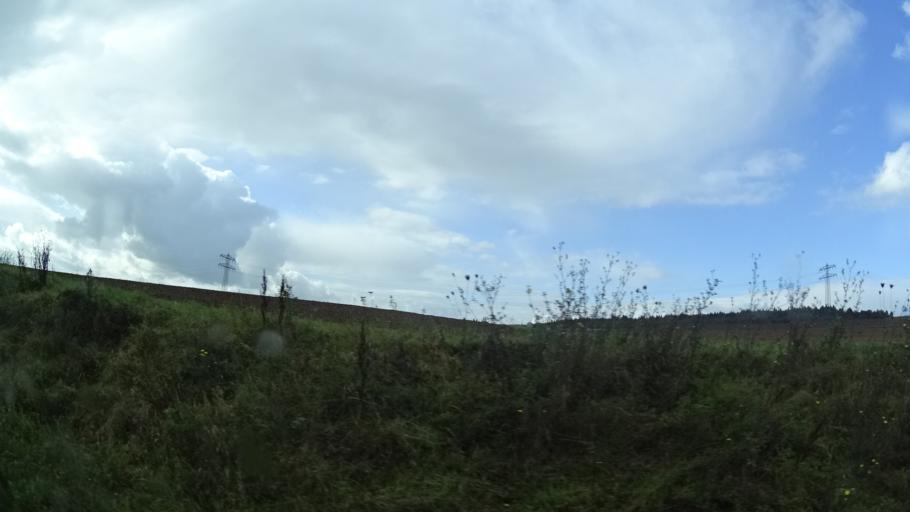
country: DE
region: Baden-Wuerttemberg
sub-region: Karlsruhe Region
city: Hardheim
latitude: 49.6332
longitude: 9.4818
